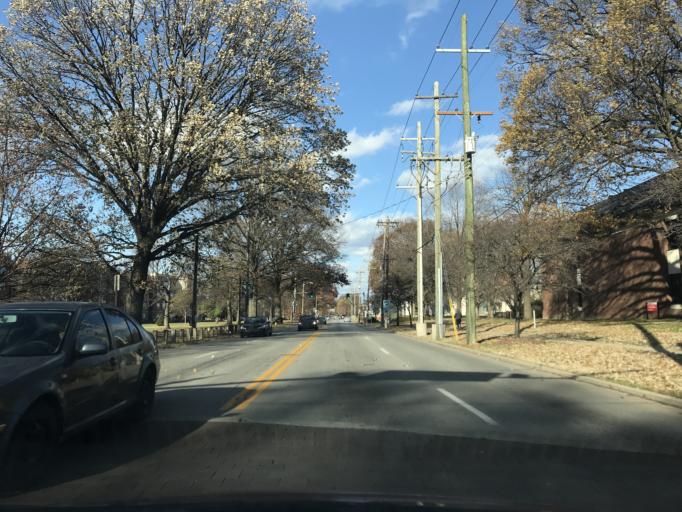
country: US
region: Kentucky
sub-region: Jefferson County
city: Audubon Park
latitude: 38.2155
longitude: -85.7621
